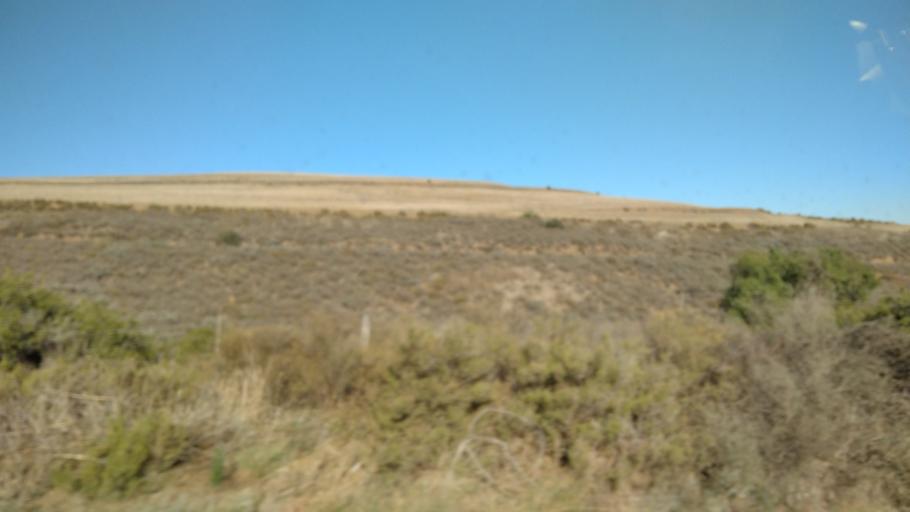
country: ZA
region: Western Cape
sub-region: West Coast District Municipality
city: Malmesbury
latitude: -33.3821
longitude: 18.6692
